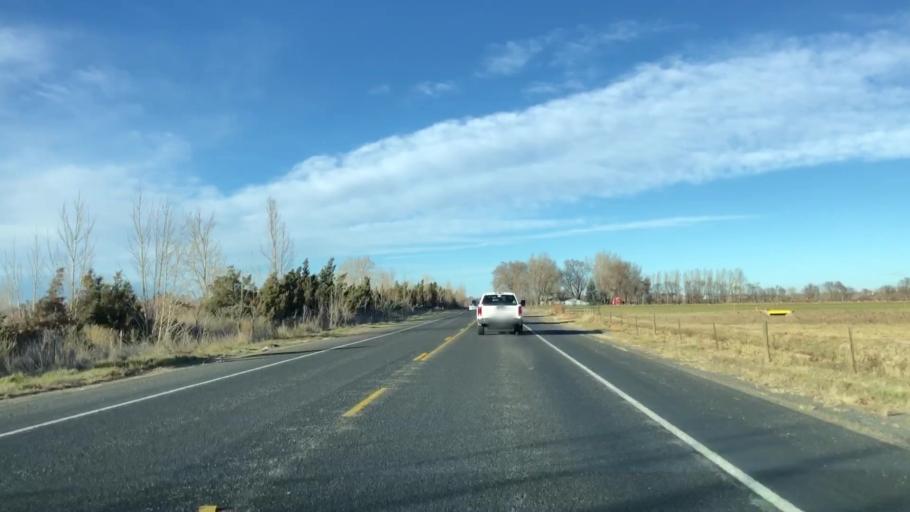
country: US
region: Colorado
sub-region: Weld County
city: Windsor
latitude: 40.5048
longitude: -104.9818
